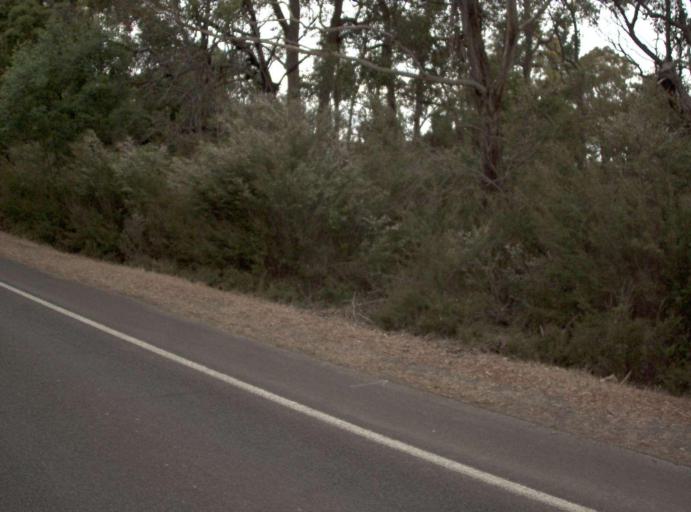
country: AU
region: Victoria
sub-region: Wellington
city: Sale
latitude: -38.5199
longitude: 146.8784
